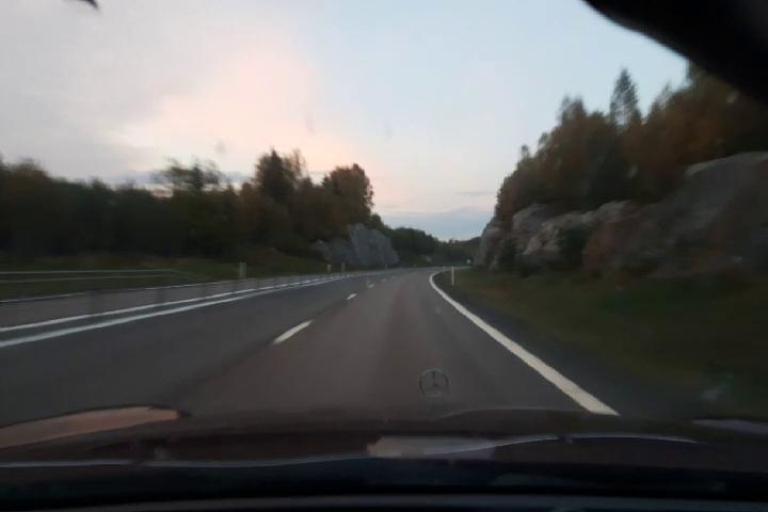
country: SE
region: Vaesternorrland
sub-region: Haernoesands Kommun
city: Haernoesand
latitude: 62.8403
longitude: 17.9753
